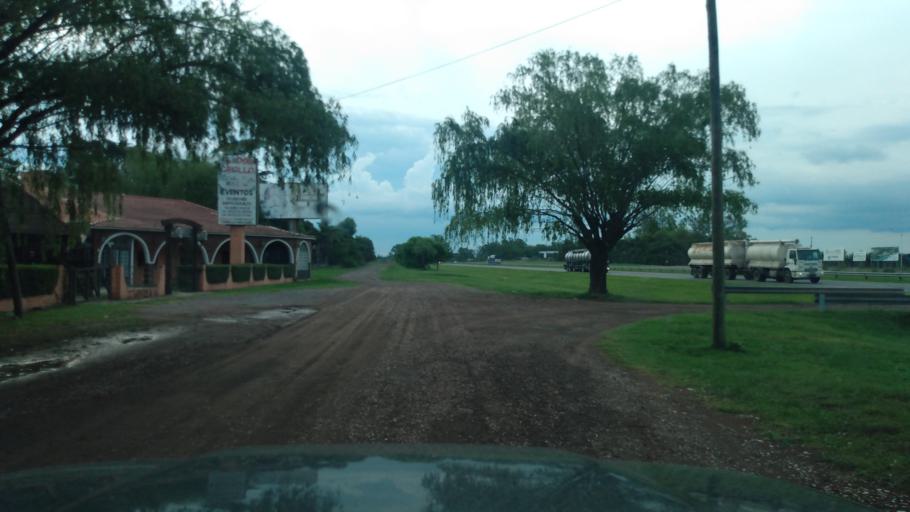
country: AR
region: Buenos Aires
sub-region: Partido de Lujan
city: Lujan
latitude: -34.5448
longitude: -59.1291
